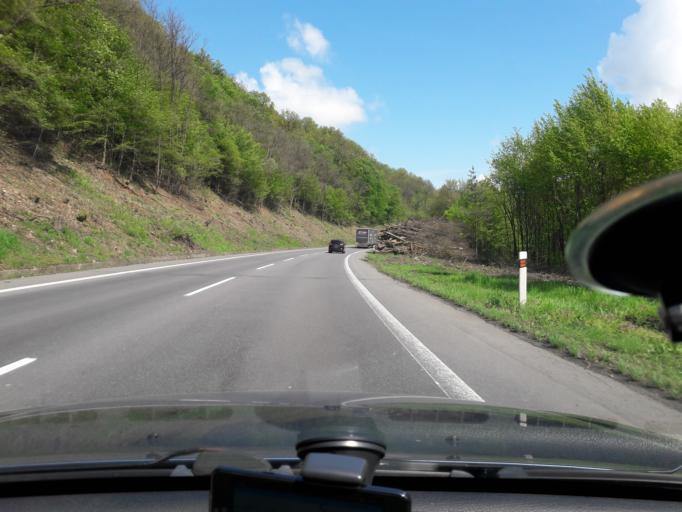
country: SK
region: Banskobystricky
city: Krupina
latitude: 48.3990
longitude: 19.0847
